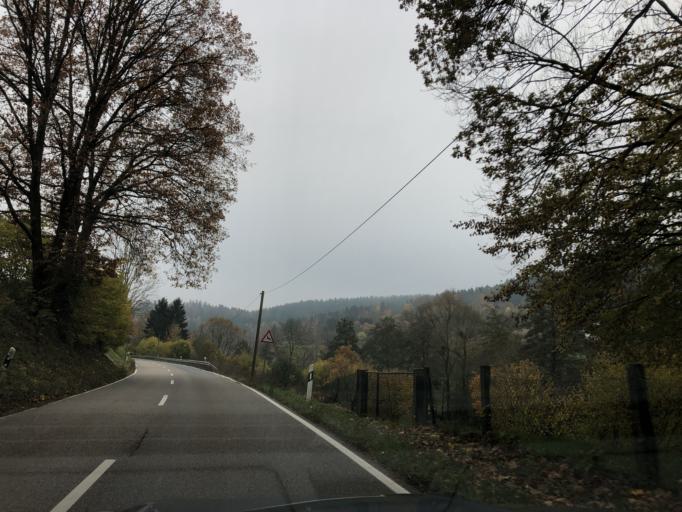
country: DE
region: Baden-Wuerttemberg
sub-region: Karlsruhe Region
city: Heiligkreuzsteinach
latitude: 49.4810
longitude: 8.7951
